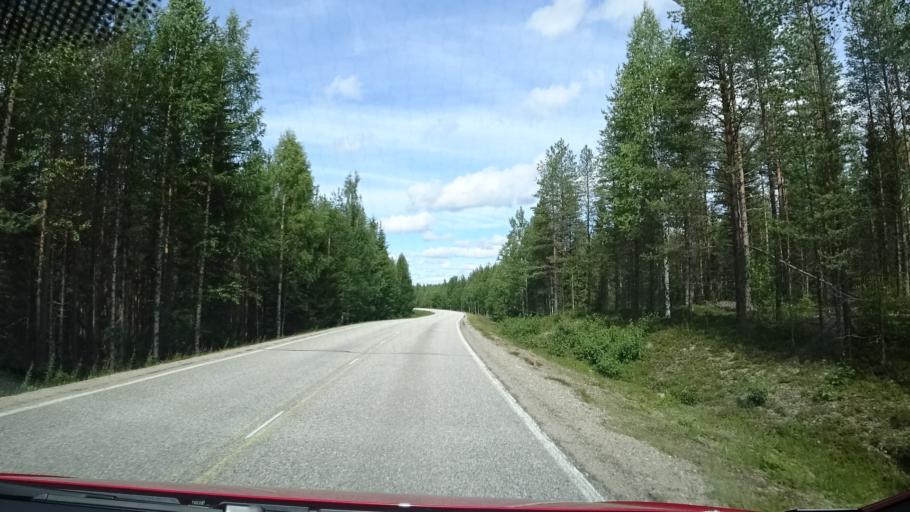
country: FI
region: Kainuu
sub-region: Kehys-Kainuu
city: Kuhmo
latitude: 64.4487
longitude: 29.7864
